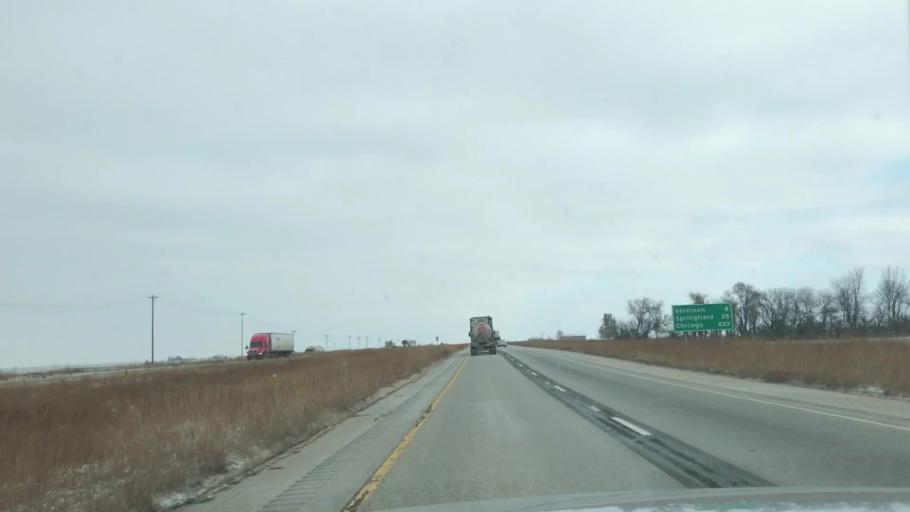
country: US
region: Illinois
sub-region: Sangamon County
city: Divernon
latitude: 39.4592
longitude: -89.6442
